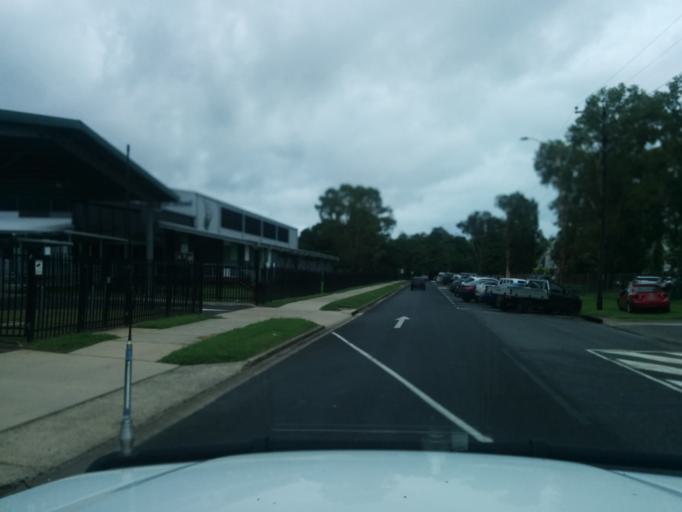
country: AU
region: Queensland
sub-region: Cairns
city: Cairns
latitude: -16.9217
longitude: 145.7537
